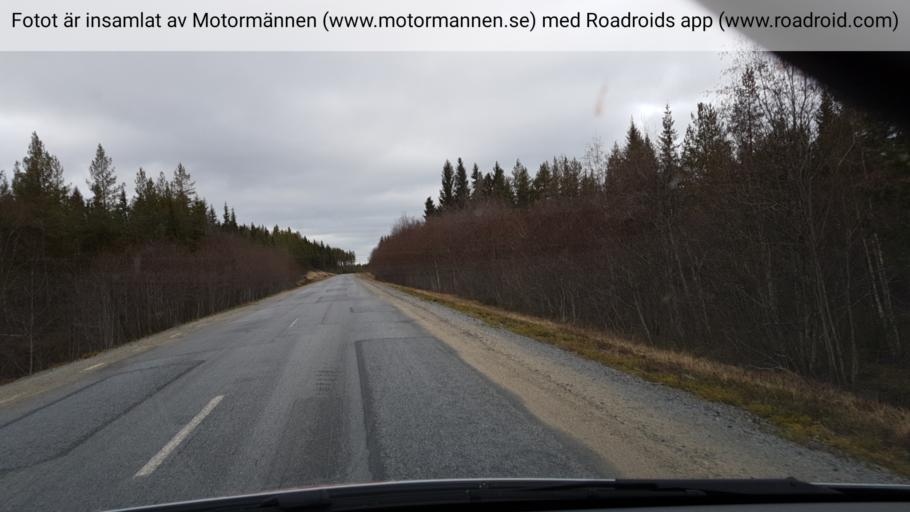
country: SE
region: Vaesternorrland
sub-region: OErnskoeldsviks Kommun
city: Bredbyn
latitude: 63.9530
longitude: 18.4819
